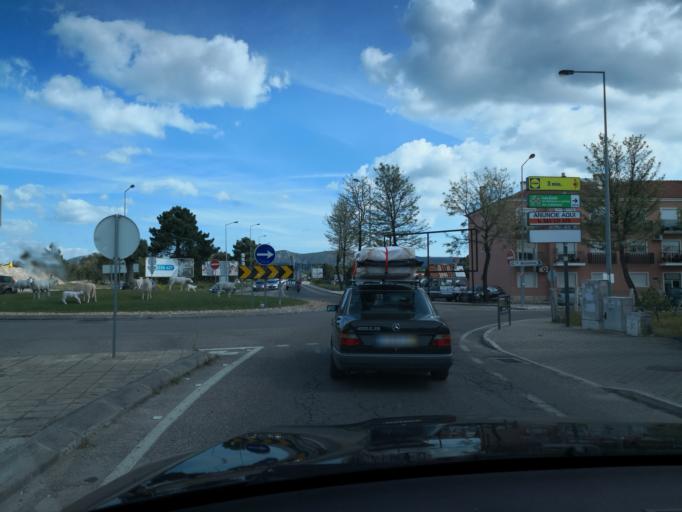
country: PT
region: Setubal
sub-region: Palmela
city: Quinta do Anjo
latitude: 38.5353
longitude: -9.0236
